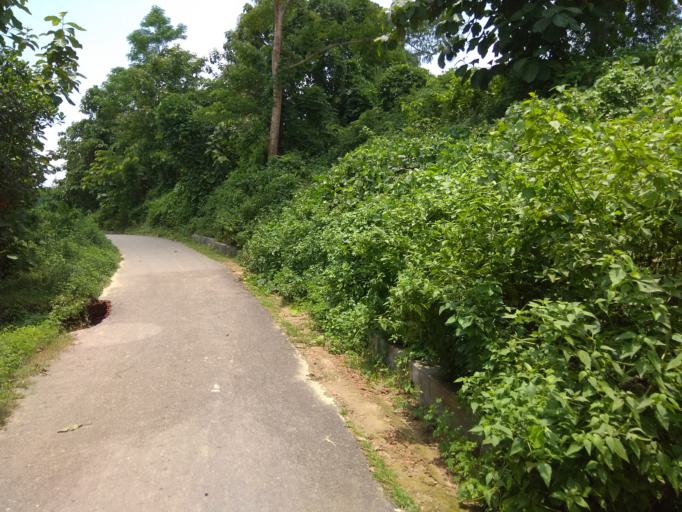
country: BD
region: Chittagong
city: Manikchari
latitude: 22.8888
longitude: 91.9226
